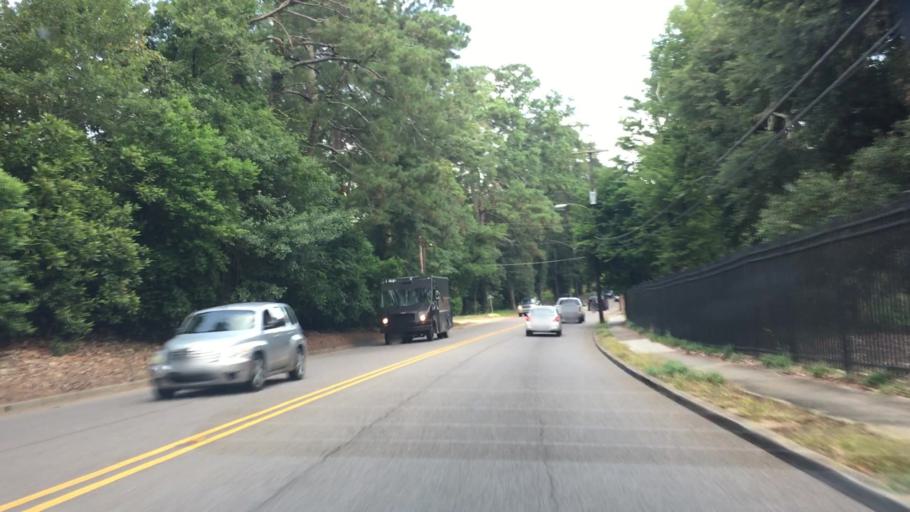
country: US
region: South Carolina
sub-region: Aiken County
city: Aiken
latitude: 33.5473
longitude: -81.7212
